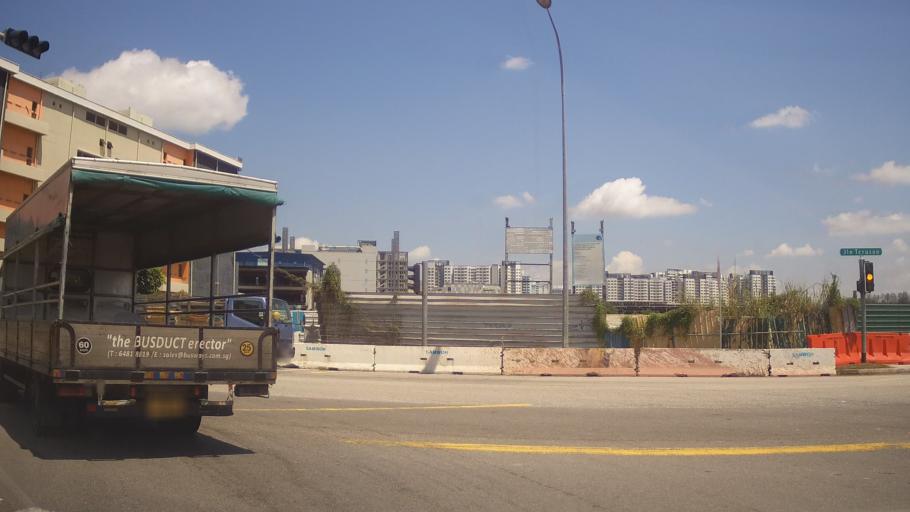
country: SG
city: Singapore
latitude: 1.3202
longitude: 103.7232
